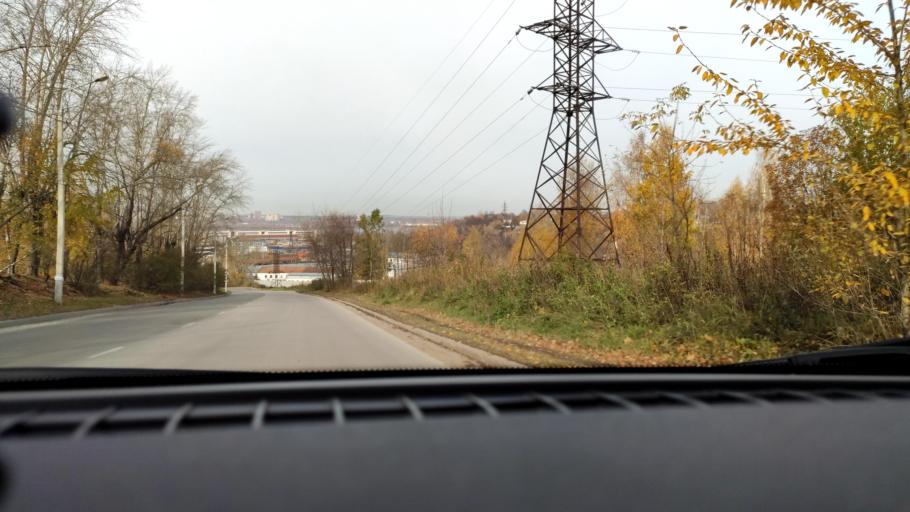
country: RU
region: Perm
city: Perm
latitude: 58.0690
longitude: 56.3546
